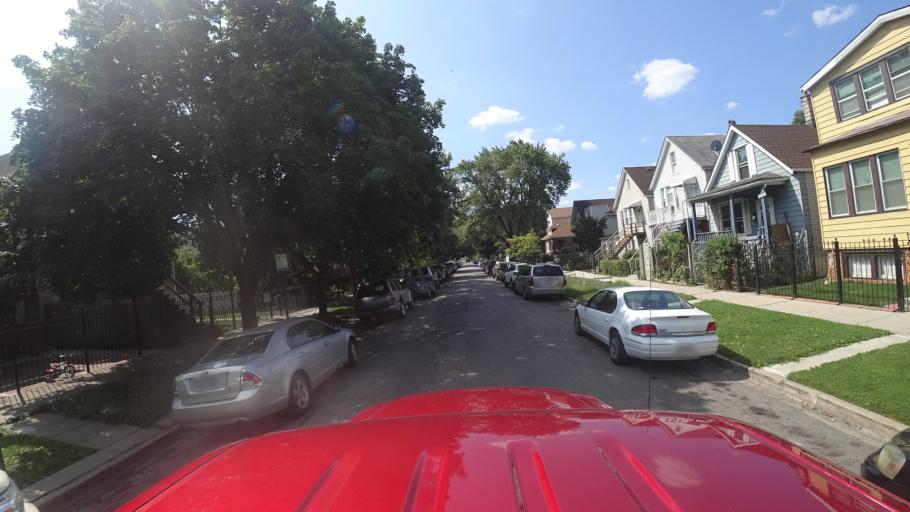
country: US
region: Illinois
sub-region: Cook County
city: Chicago
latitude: 41.7973
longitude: -87.6866
